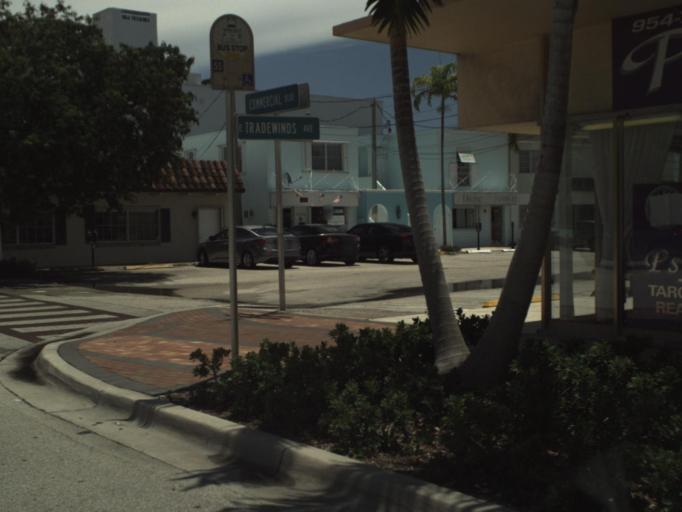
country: US
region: Florida
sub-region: Broward County
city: Lauderdale-by-the-Sea
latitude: 26.1899
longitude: -80.1004
